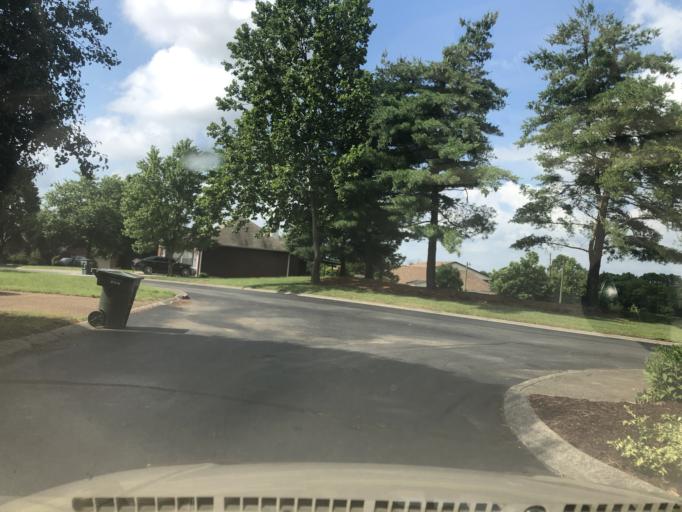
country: US
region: Tennessee
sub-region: Davidson County
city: Lakewood
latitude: 36.2253
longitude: -86.6016
